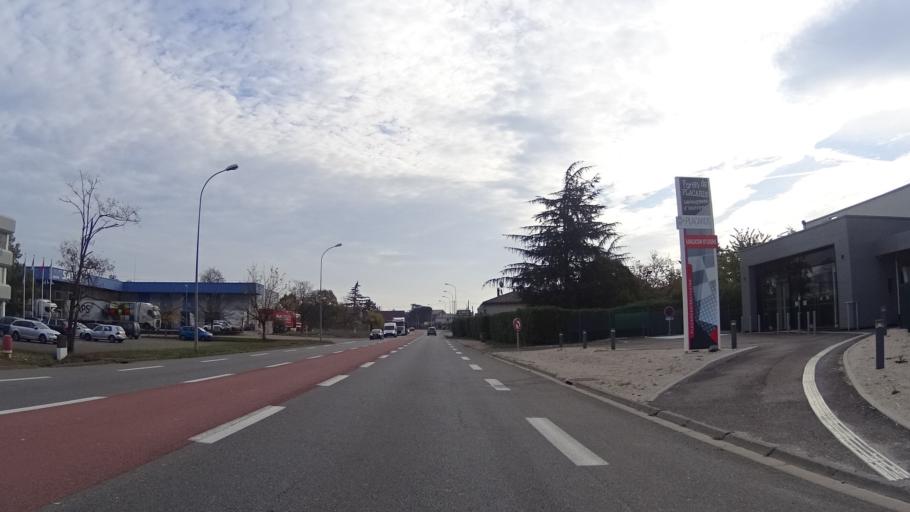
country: FR
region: Aquitaine
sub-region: Departement du Lot-et-Garonne
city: Boe
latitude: 44.1649
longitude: 0.5973
